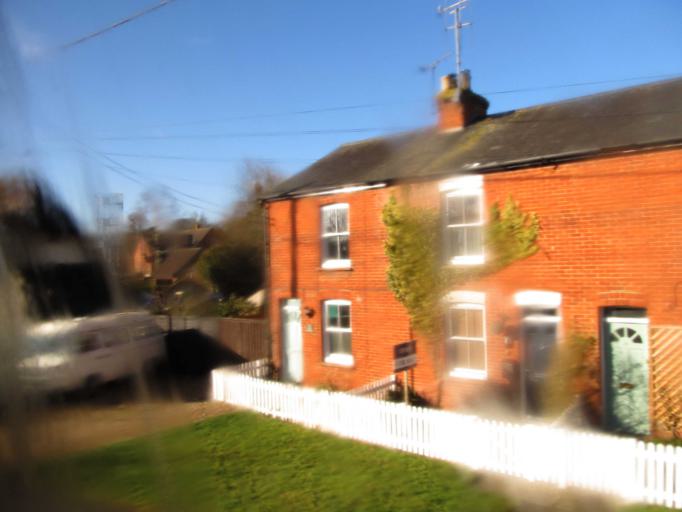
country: GB
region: England
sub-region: Hampshire
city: Kings Worthy
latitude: 51.1545
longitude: -1.3378
